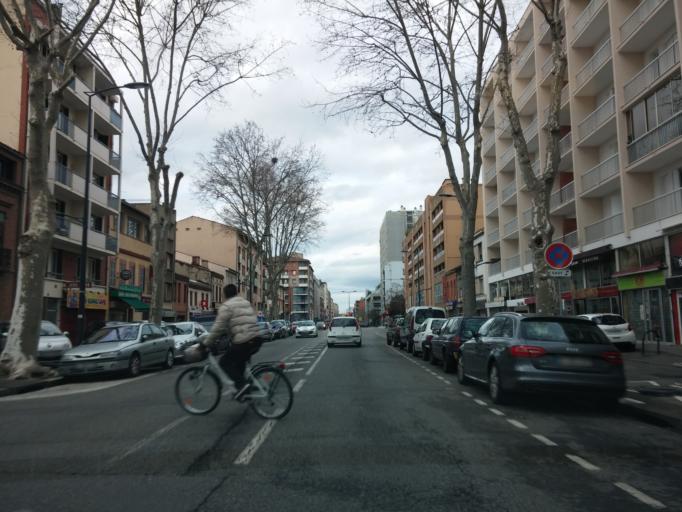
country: FR
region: Midi-Pyrenees
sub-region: Departement de la Haute-Garonne
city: Toulouse
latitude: 43.5829
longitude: 1.4484
